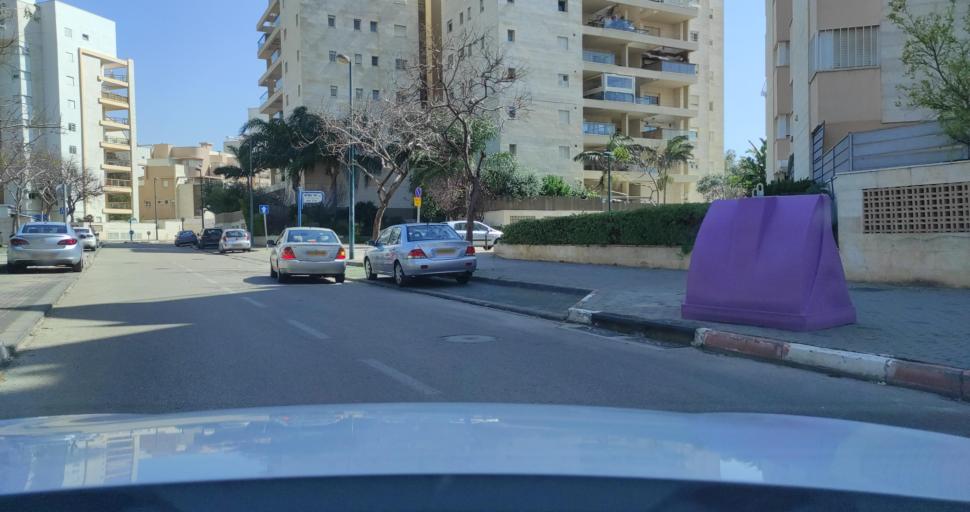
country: IL
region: Central District
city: Nordiyya
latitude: 32.3084
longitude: 34.8708
